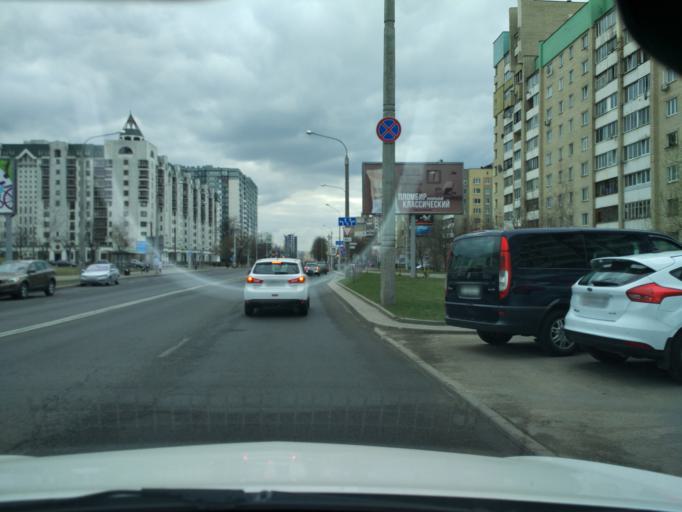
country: BY
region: Minsk
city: Minsk
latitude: 53.9341
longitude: 27.5910
